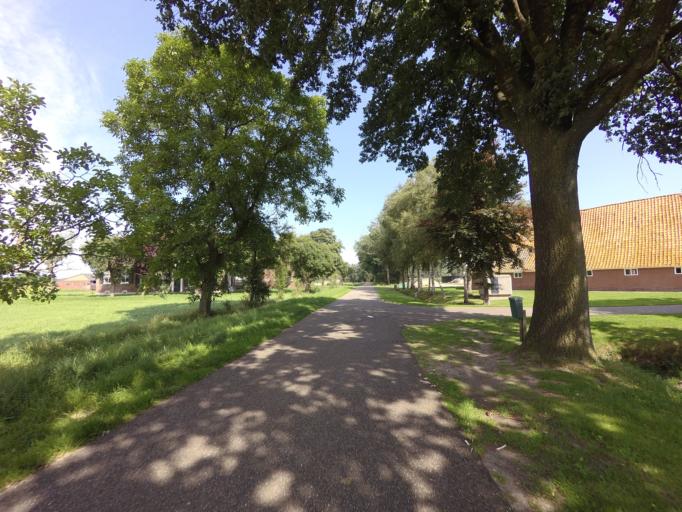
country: NL
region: Overijssel
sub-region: Gemeente Hof van Twente
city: Hengevelde
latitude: 52.1767
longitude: 6.6262
